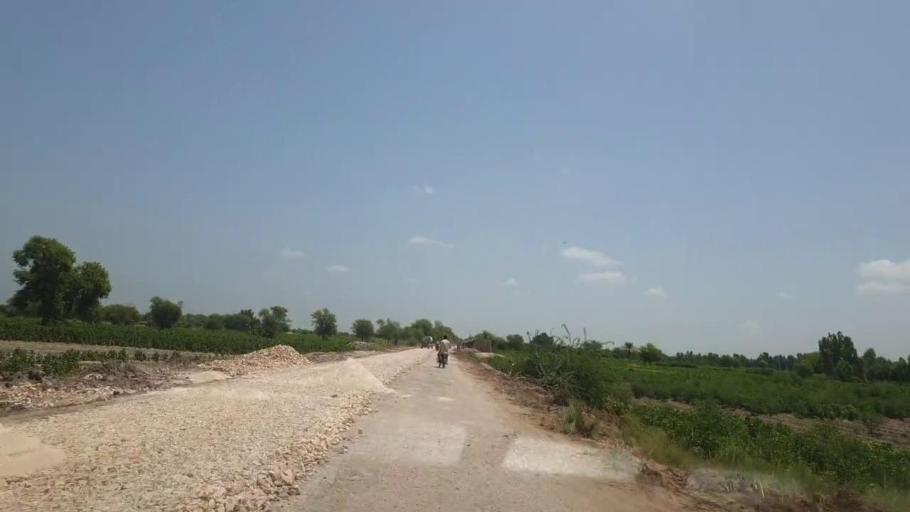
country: PK
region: Sindh
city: Pano Aqil
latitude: 27.6661
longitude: 69.1794
